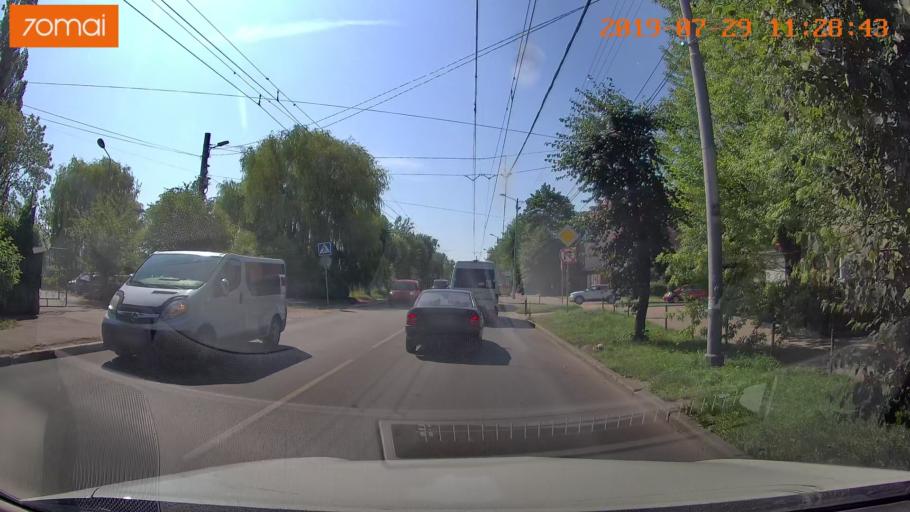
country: RU
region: Kaliningrad
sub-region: Gorod Kaliningrad
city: Kaliningrad
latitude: 54.6867
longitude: 20.5329
